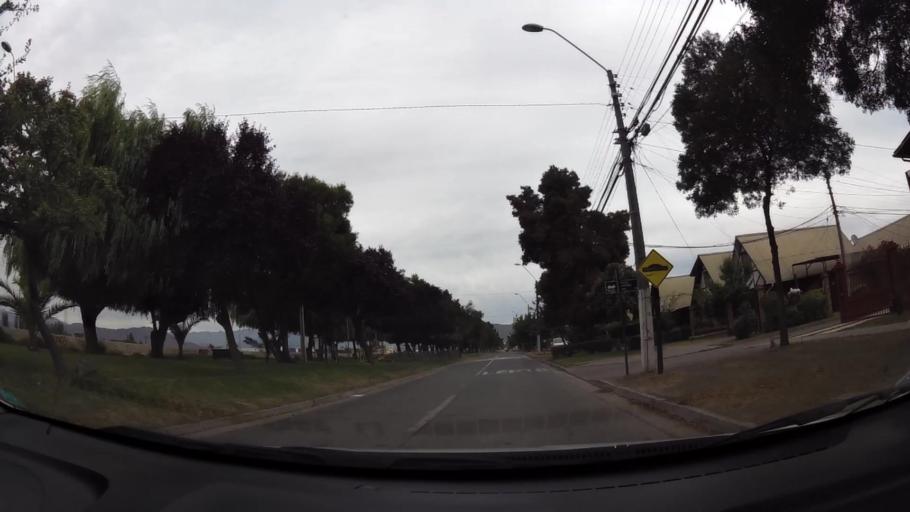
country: CL
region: O'Higgins
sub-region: Provincia de Cachapoal
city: Rancagua
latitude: -34.1504
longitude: -70.7289
